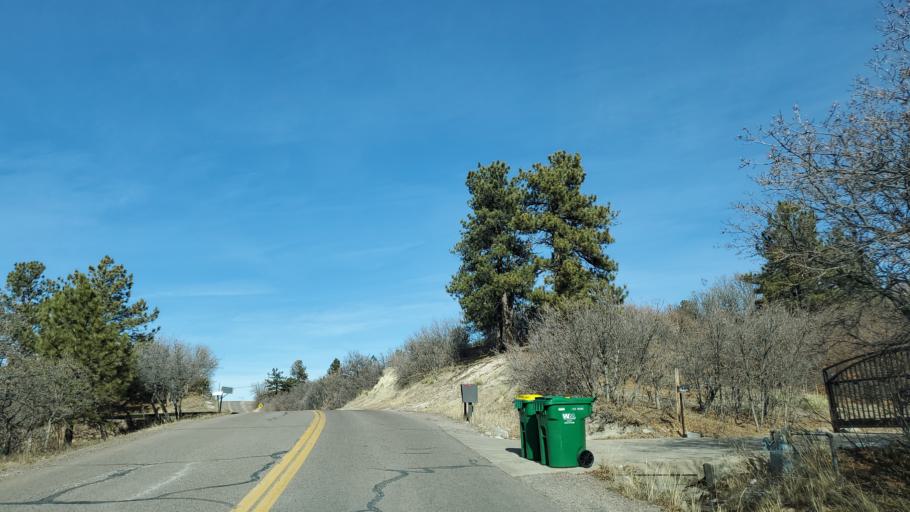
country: US
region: Colorado
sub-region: Douglas County
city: Castle Pines
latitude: 39.4451
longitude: -104.8713
